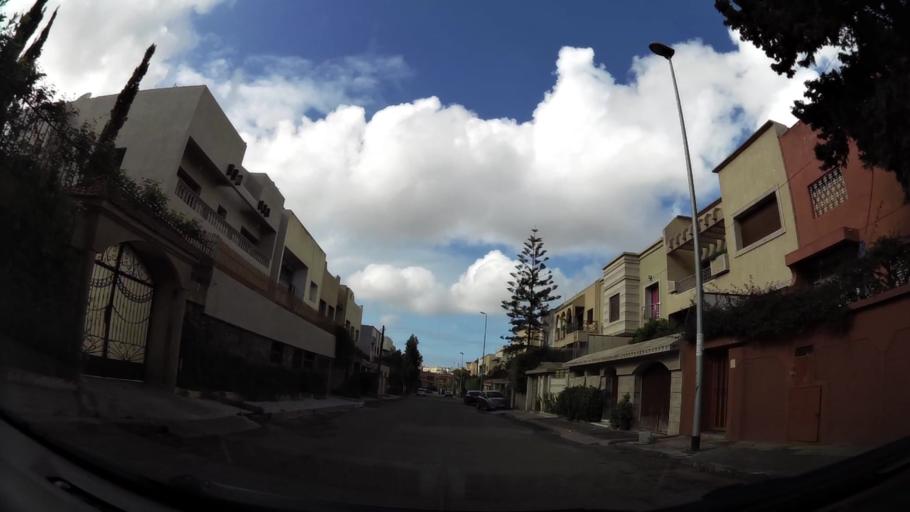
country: MA
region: Grand Casablanca
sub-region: Casablanca
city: Casablanca
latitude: 33.5470
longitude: -7.6030
